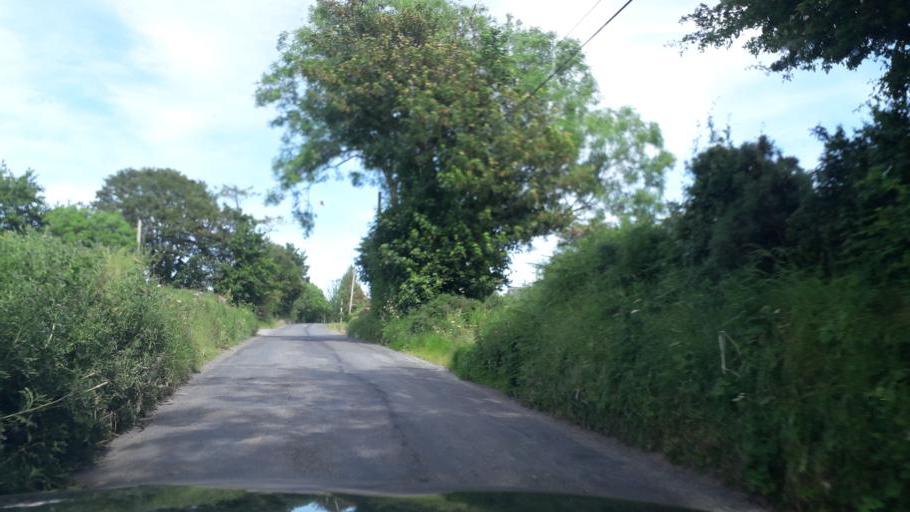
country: IE
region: Leinster
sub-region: Loch Garman
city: Castlebridge
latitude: 52.4142
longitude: -6.4160
